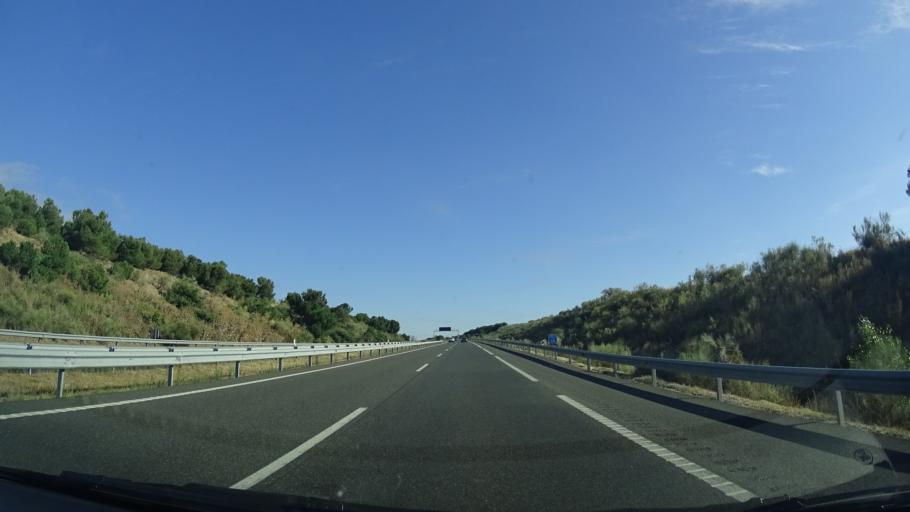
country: ES
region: Castille and Leon
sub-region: Provincia de Avila
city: Sanchidrian
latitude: 40.8723
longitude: -4.5669
